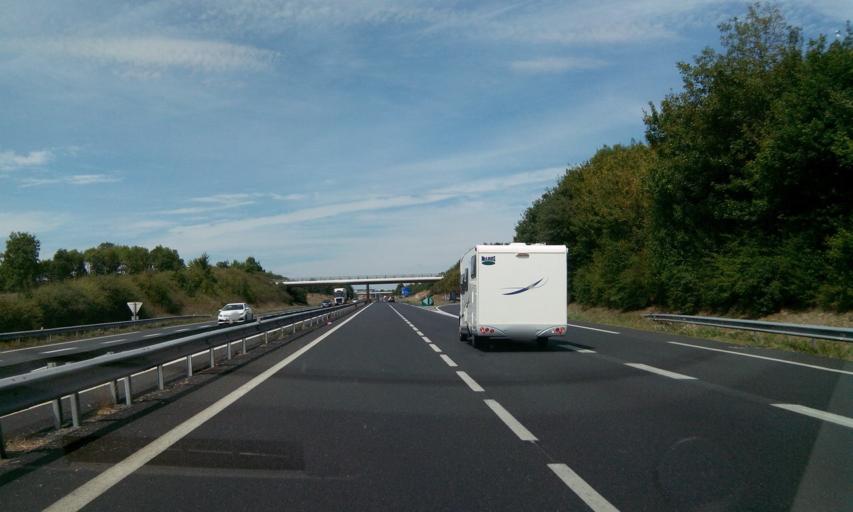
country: FR
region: Pays de la Loire
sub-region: Departement de la Vendee
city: Les Essarts
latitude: 46.7902
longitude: -1.1979
